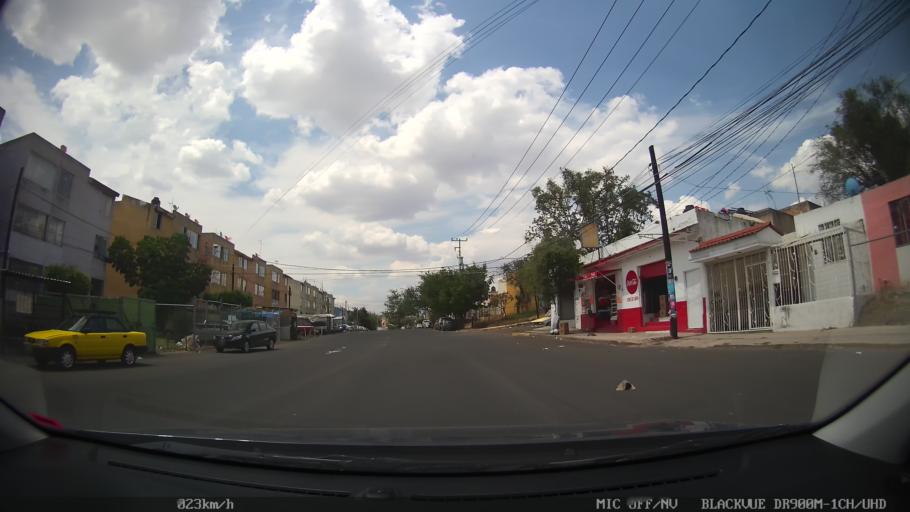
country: MX
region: Jalisco
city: Tonala
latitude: 20.6222
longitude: -103.2523
